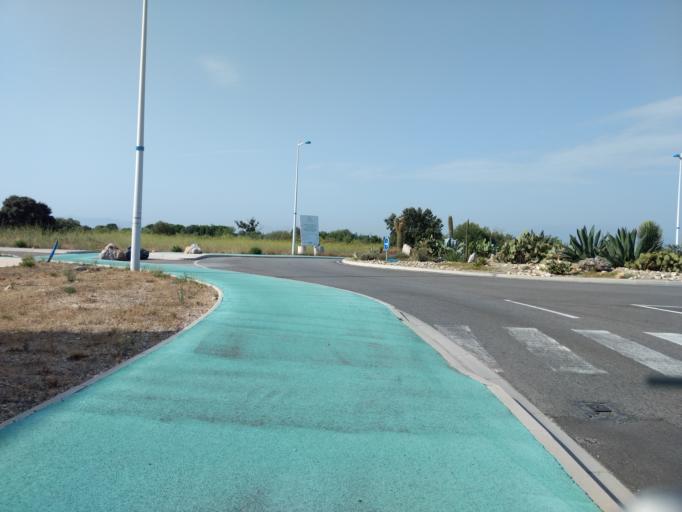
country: FR
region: Languedoc-Roussillon
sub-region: Departement des Pyrenees-Orientales
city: Pia
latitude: 42.7718
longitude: 2.9145
